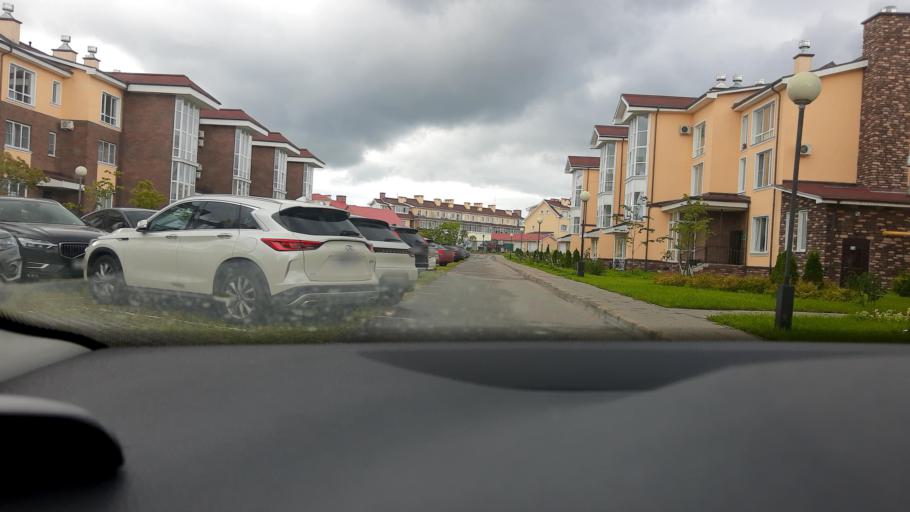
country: RU
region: Moskovskaya
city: Krasnogorsk
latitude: 55.8593
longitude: 37.3258
